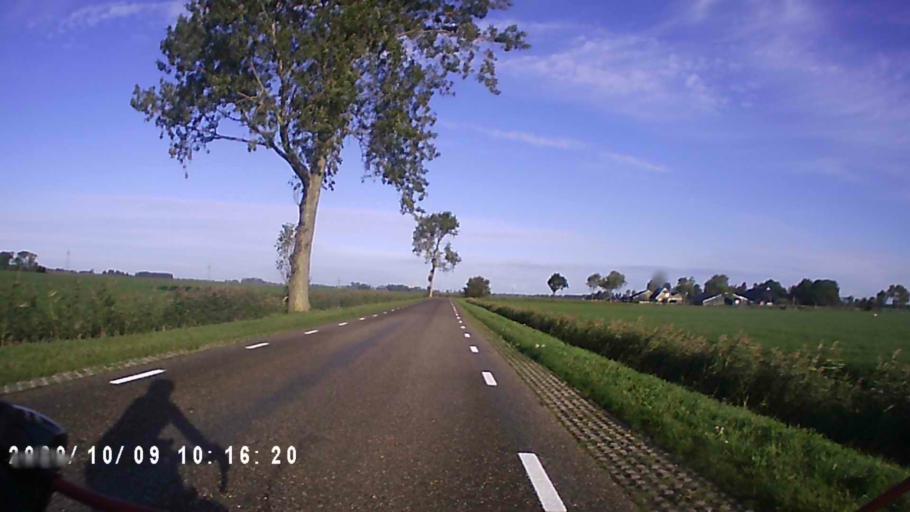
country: NL
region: Groningen
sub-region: Gemeente Winsum
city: Winsum
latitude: 53.3093
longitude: 6.5029
